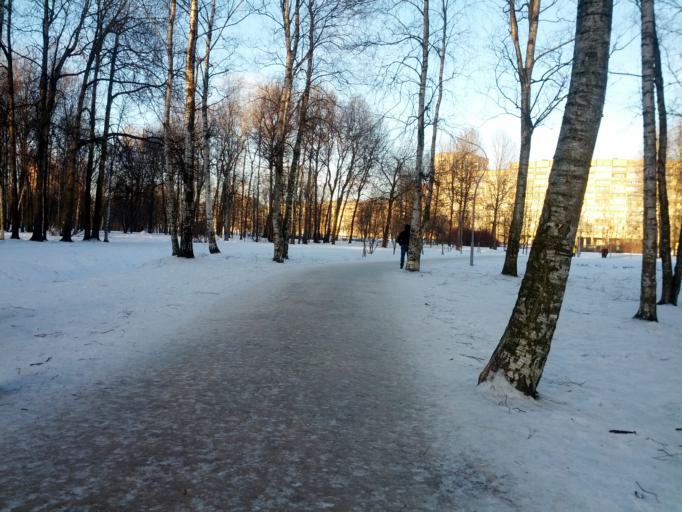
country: RU
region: St.-Petersburg
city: Krasnogvargeisky
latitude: 59.9098
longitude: 30.4856
